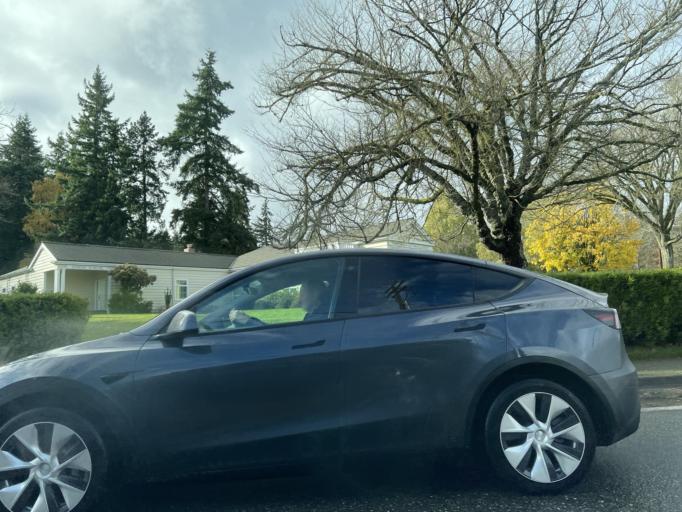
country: US
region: Washington
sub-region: Kitsap County
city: Bainbridge Island
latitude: 47.6354
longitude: -122.5210
